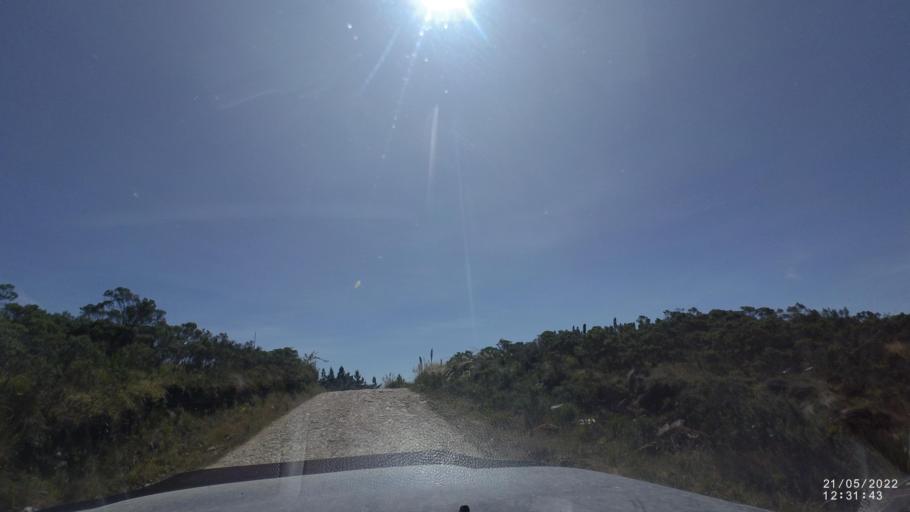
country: BO
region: Cochabamba
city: Colomi
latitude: -17.2099
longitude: -65.9146
